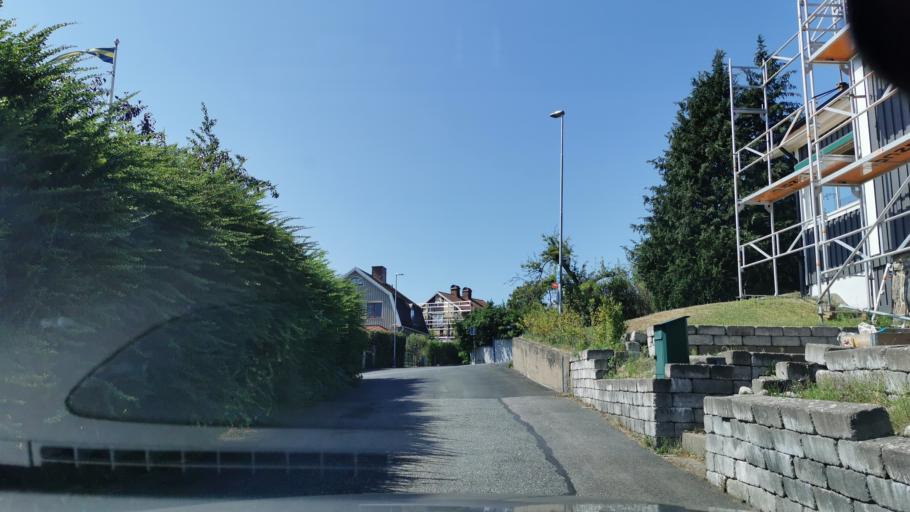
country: SE
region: Vaestra Goetaland
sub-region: Molndal
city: Moelndal
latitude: 57.6757
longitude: 11.9992
